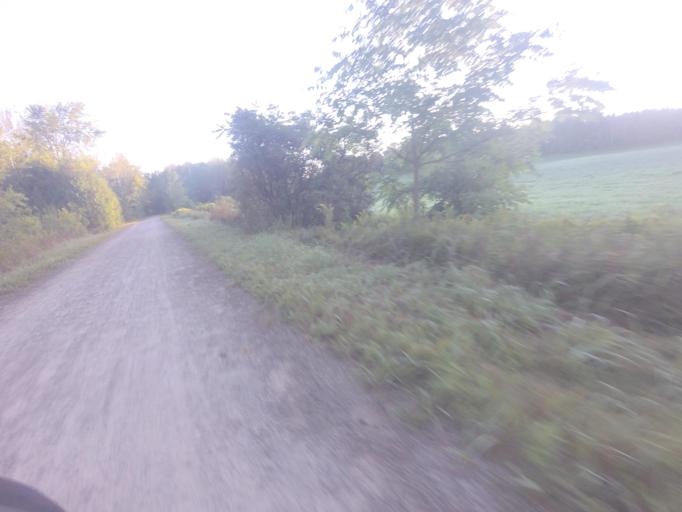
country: CA
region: Ontario
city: Bradford West Gwillimbury
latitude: 44.0121
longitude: -79.8087
